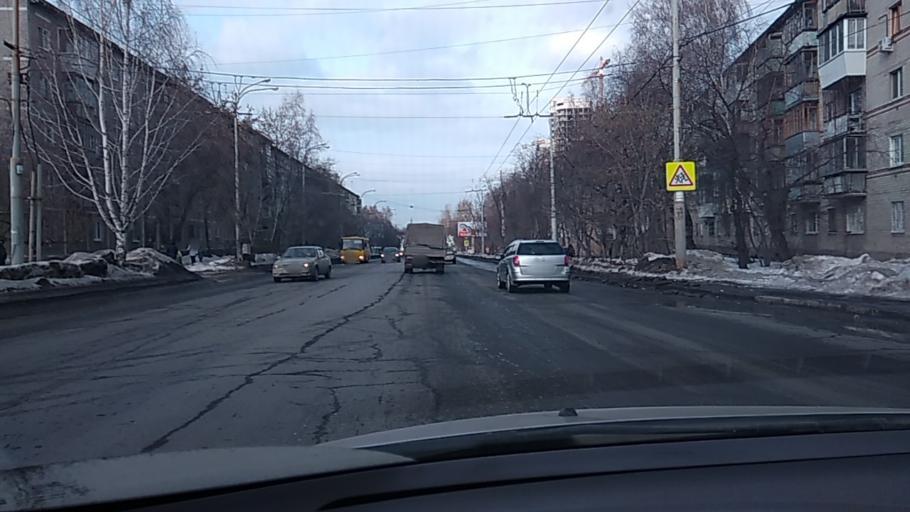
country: RU
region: Sverdlovsk
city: Yekaterinburg
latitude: 56.8585
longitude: 60.6537
